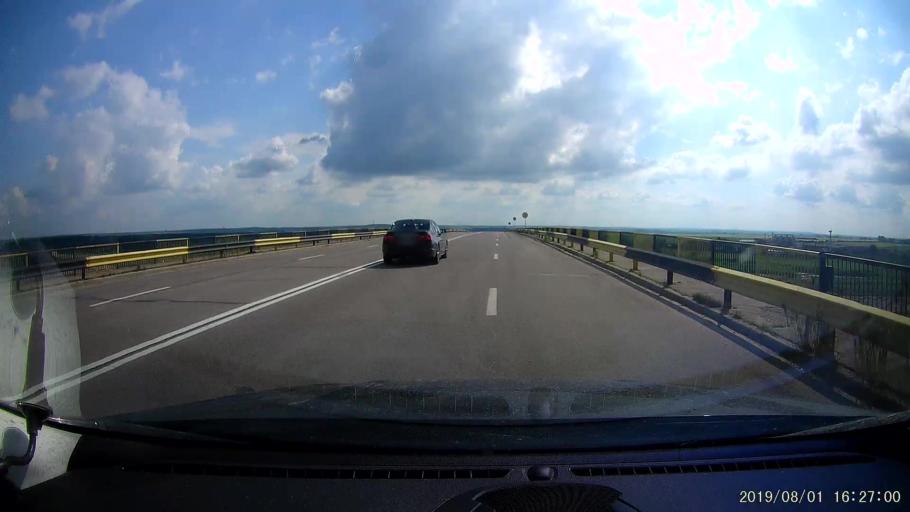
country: RO
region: Calarasi
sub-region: Municipiul Calarasi
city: Calarasi
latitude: 44.1698
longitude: 27.3138
